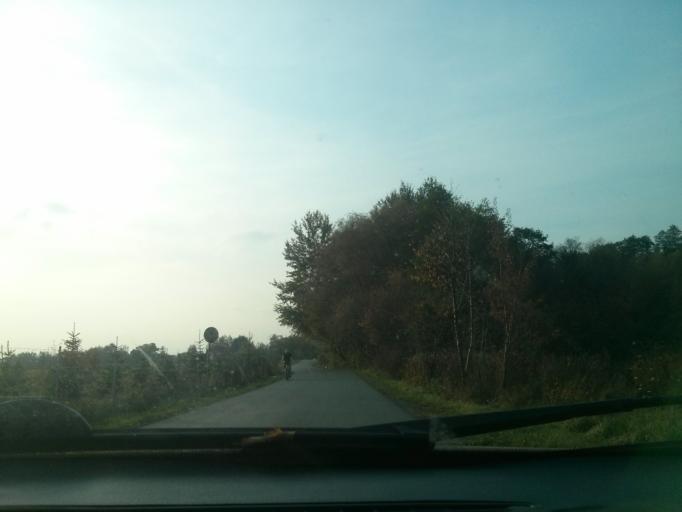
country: PL
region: Masovian Voivodeship
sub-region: Powiat piaseczynski
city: Konstancin-Jeziorna
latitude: 52.1227
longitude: 21.1564
